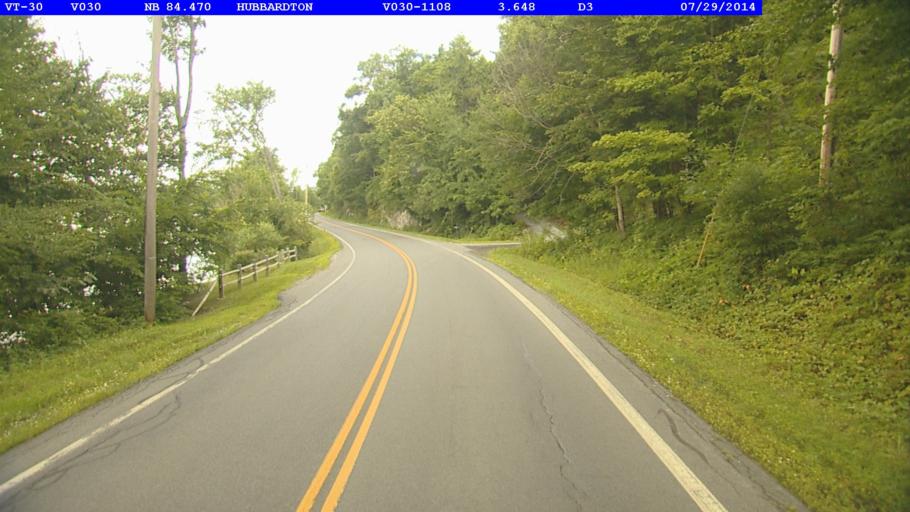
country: US
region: Vermont
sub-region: Rutland County
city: Brandon
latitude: 43.7301
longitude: -73.1806
